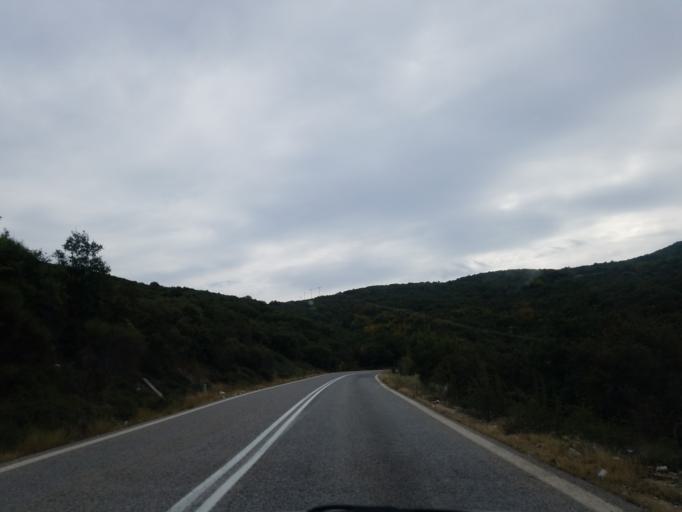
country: GR
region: Central Greece
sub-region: Nomos Fthiotidos
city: Domokos
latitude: 39.1479
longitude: 22.3076
